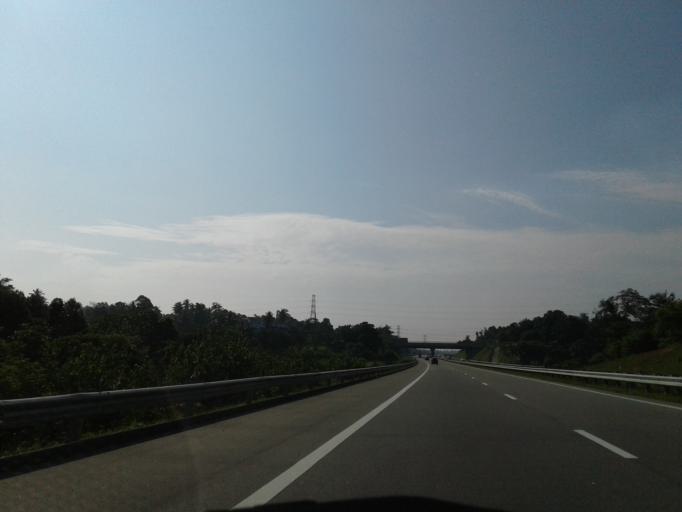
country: LK
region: Western
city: Kelaniya
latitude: 6.9741
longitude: 79.9706
